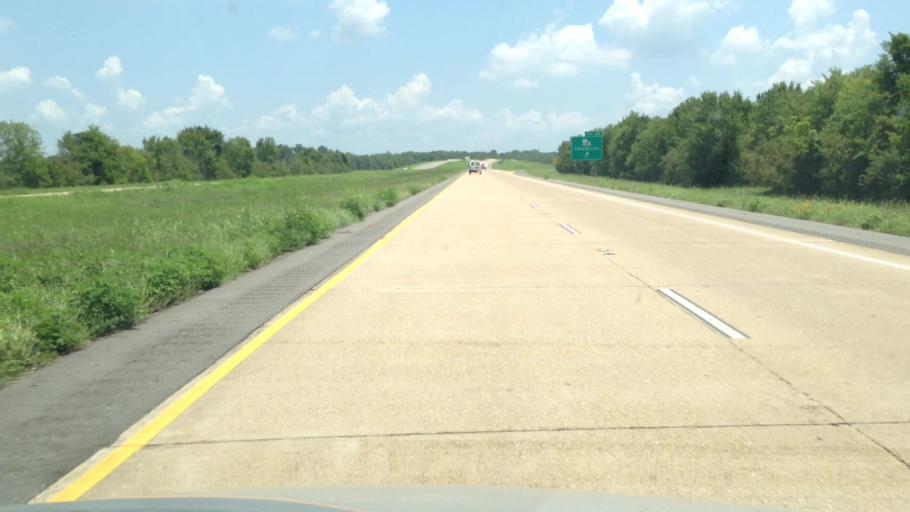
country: US
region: Louisiana
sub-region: Rapides Parish
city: Lecompte
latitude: 30.9905
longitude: -92.3154
